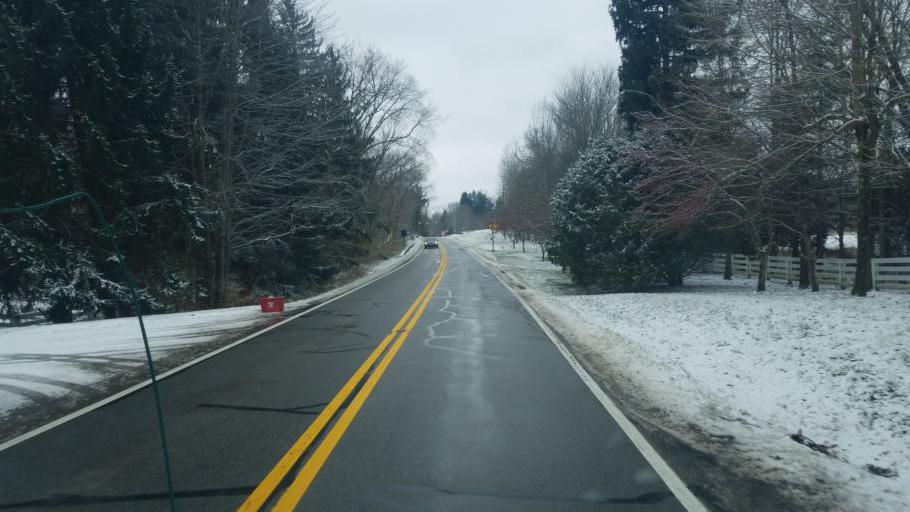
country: US
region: Ohio
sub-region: Franklin County
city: New Albany
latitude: 40.0548
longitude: -82.8019
